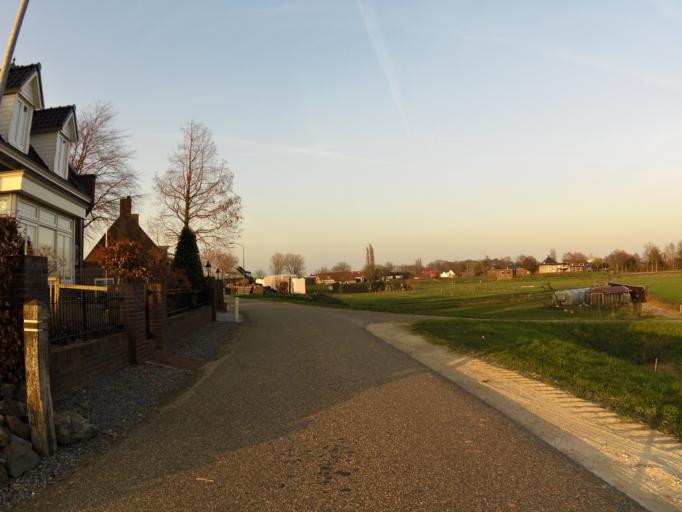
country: NL
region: Gelderland
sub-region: Gemeente Maasdriel
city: Hedel
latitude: 51.7407
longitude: 5.2599
